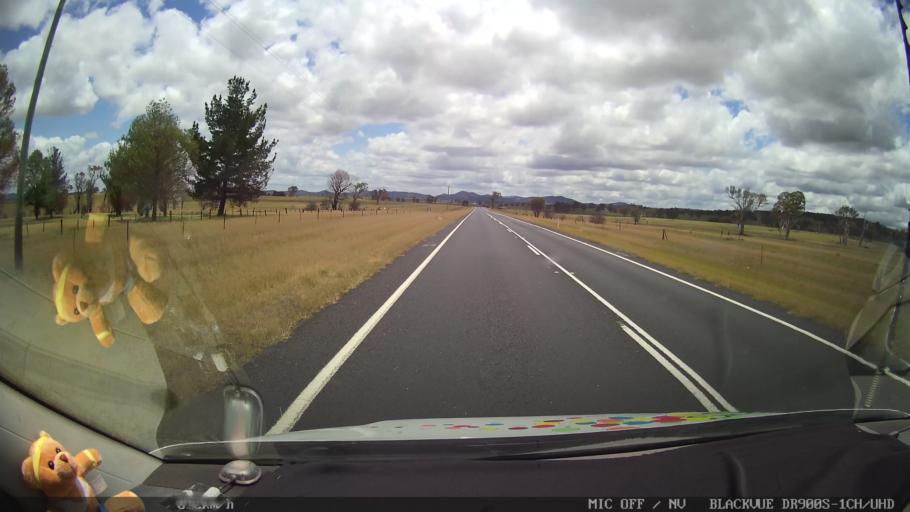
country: AU
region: New South Wales
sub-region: Glen Innes Severn
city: Glen Innes
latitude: -29.4275
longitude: 151.8572
